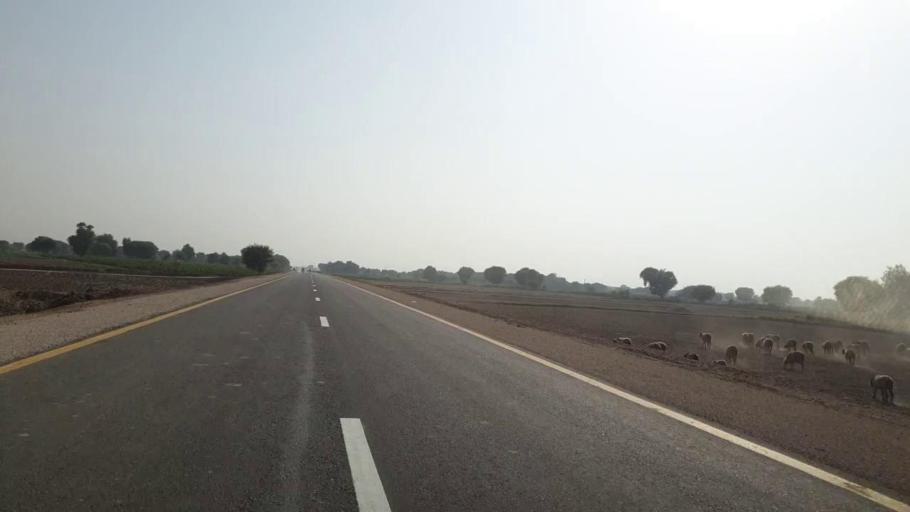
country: PK
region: Sindh
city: Bhan
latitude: 26.5248
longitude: 67.7891
